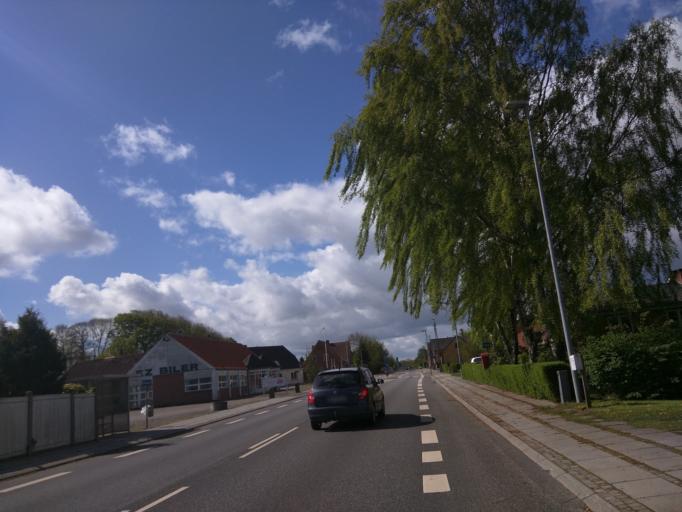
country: DK
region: Central Jutland
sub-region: Silkeborg Kommune
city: Kjellerup
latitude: 56.3349
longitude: 9.4243
